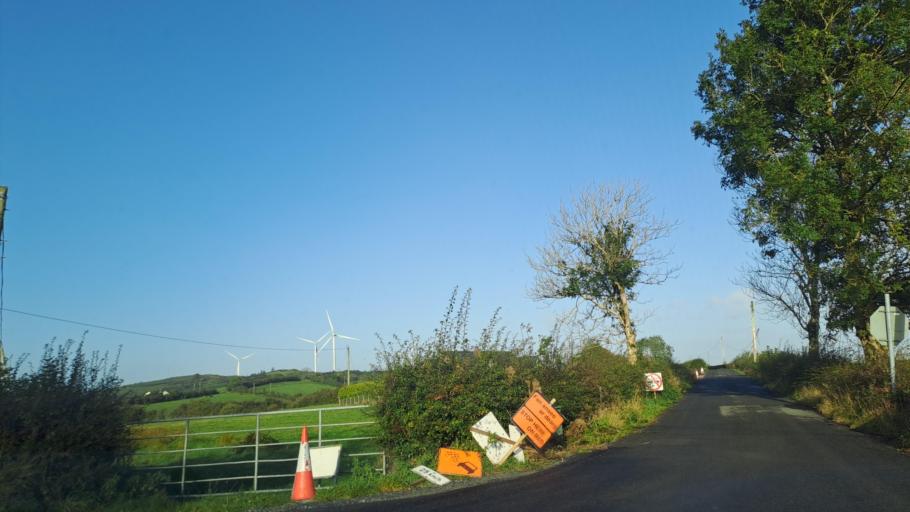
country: IE
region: Ulster
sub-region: County Monaghan
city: Castleblayney
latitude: 54.0803
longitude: -6.8479
